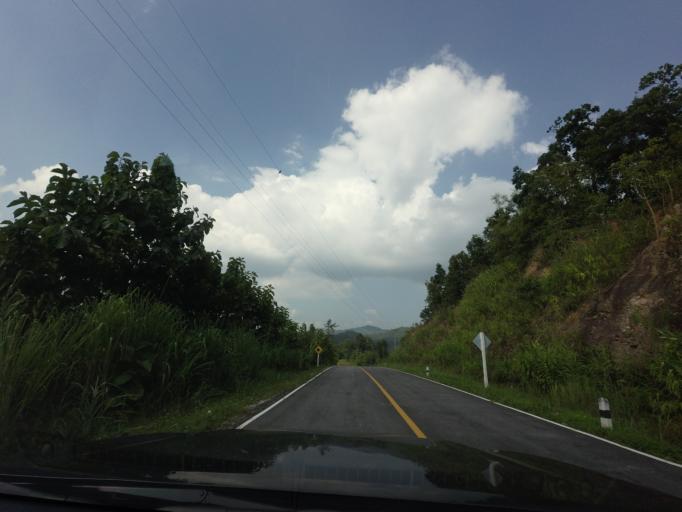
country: TH
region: Uttaradit
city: Ban Khok
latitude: 18.2276
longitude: 101.0329
